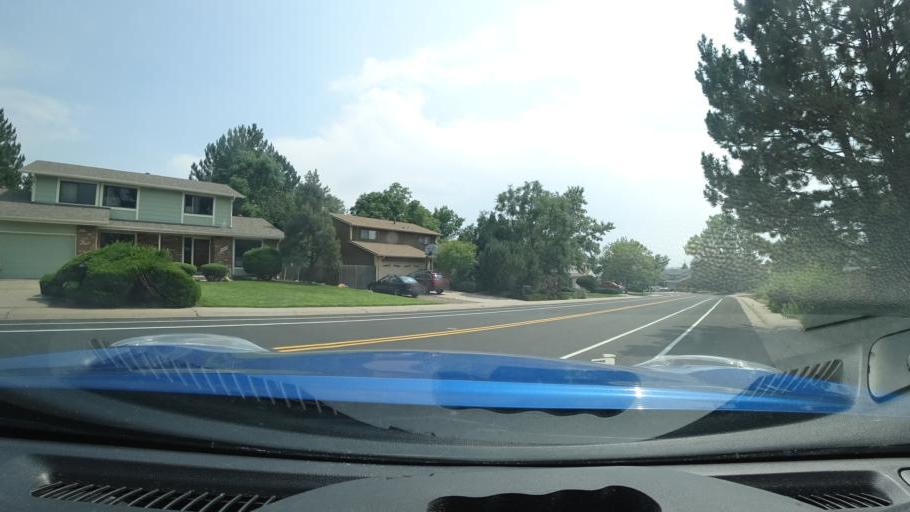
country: US
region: Colorado
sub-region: Adams County
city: Aurora
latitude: 39.6700
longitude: -104.8600
